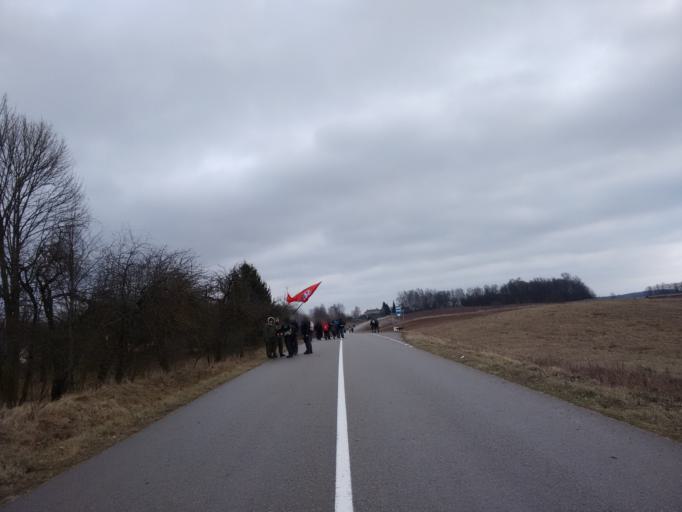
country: LT
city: Veisiejai
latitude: 54.2451
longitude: 23.8726
